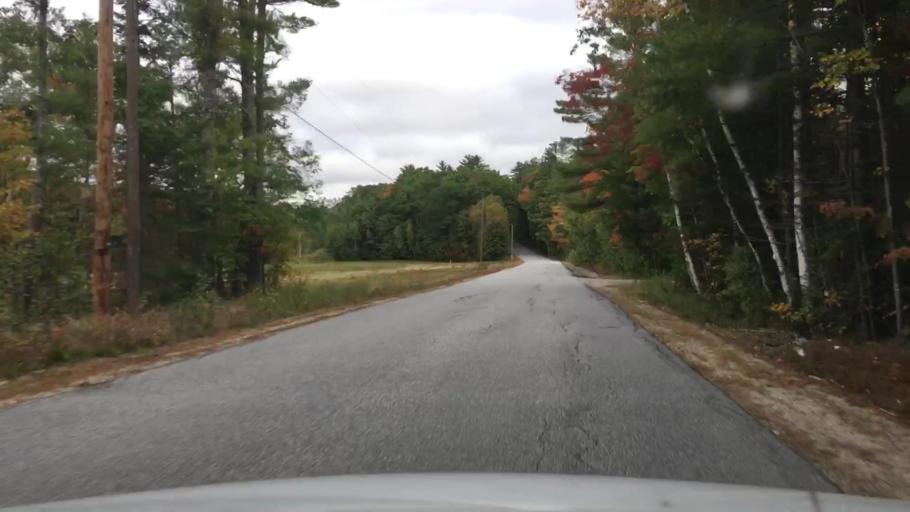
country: US
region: Maine
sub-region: Cumberland County
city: Harrison
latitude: 44.2510
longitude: -70.7223
